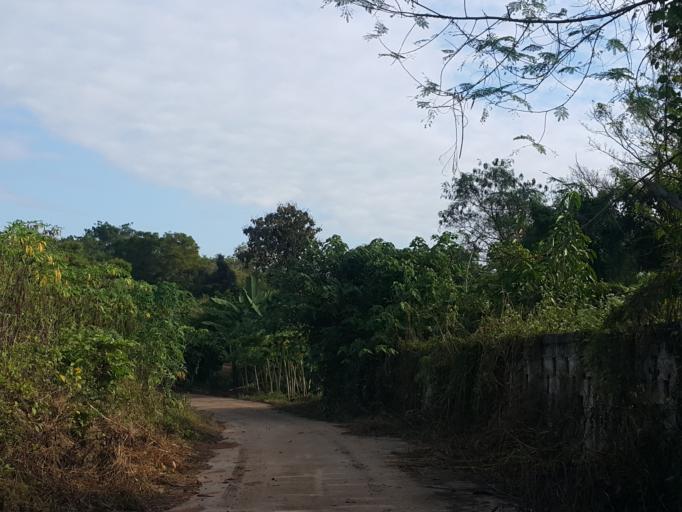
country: TH
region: Lampang
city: Mae Mo
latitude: 18.2604
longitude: 99.6040
